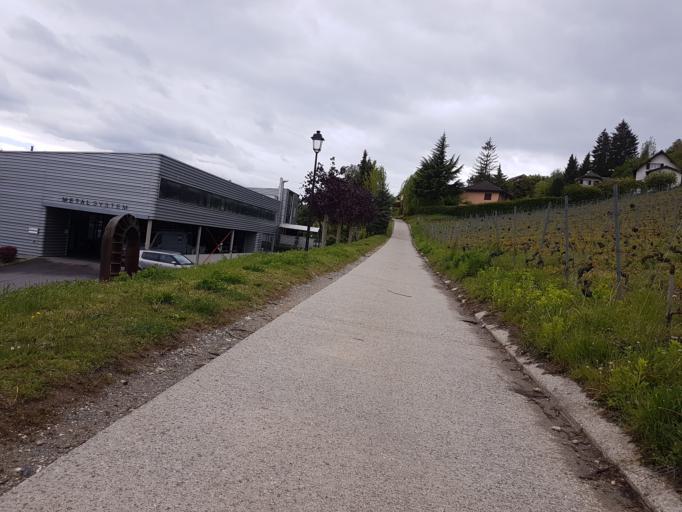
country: CH
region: Vaud
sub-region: Ouest Lausannois District
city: Bussigny
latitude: 46.5399
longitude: 6.5474
